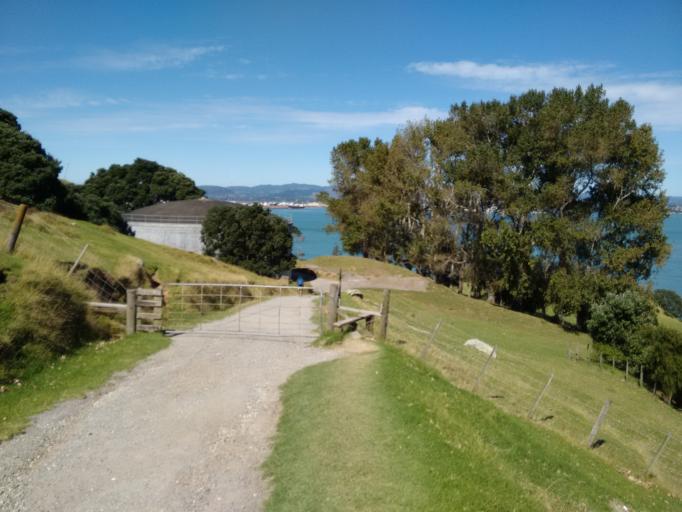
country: NZ
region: Bay of Plenty
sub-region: Tauranga City
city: Tauranga
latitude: -37.6331
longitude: 176.1695
